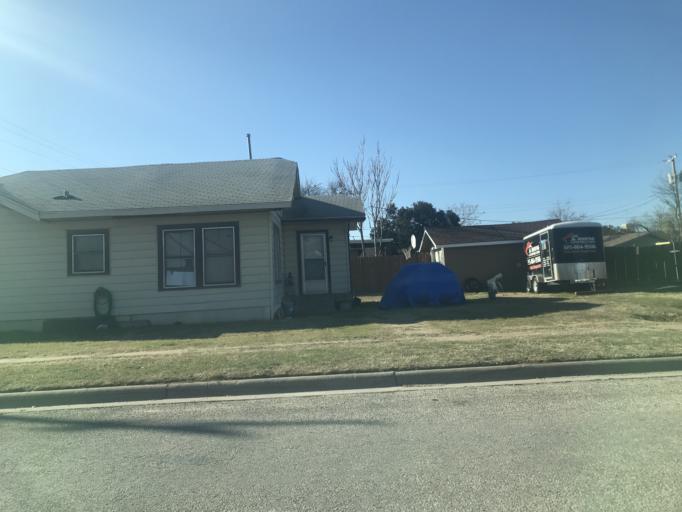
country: US
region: Texas
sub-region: Taylor County
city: Abilene
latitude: 32.4324
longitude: -99.7374
